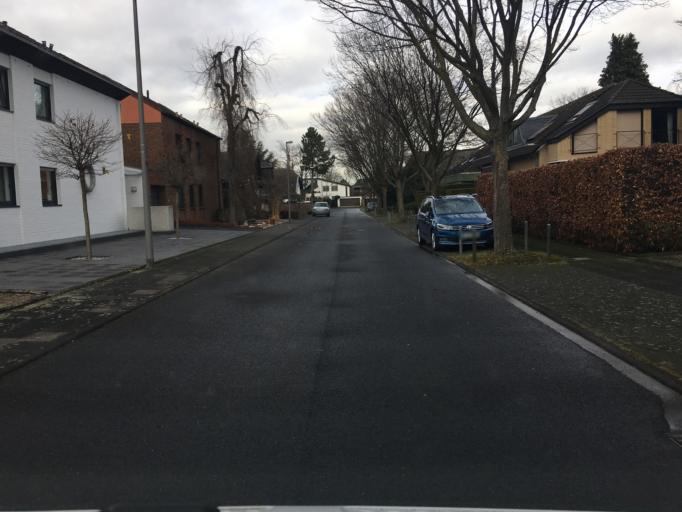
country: DE
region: North Rhine-Westphalia
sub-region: Regierungsbezirk Koln
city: Mengenich
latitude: 50.9497
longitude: 6.8610
